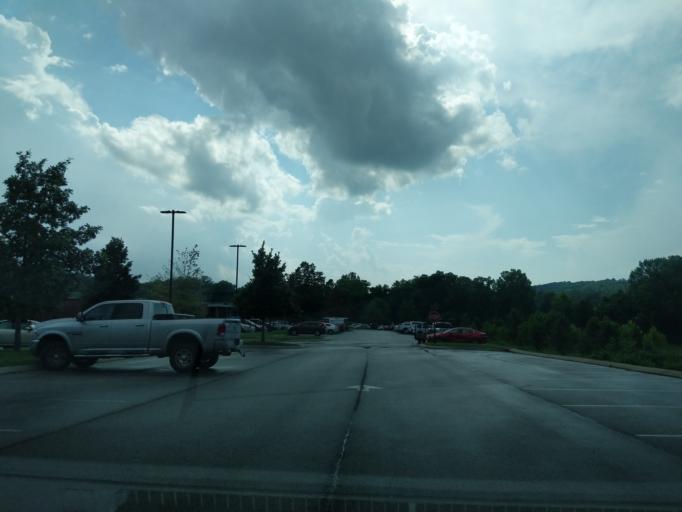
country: US
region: Tennessee
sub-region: Davidson County
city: Belle Meade
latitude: 36.0426
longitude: -86.9526
